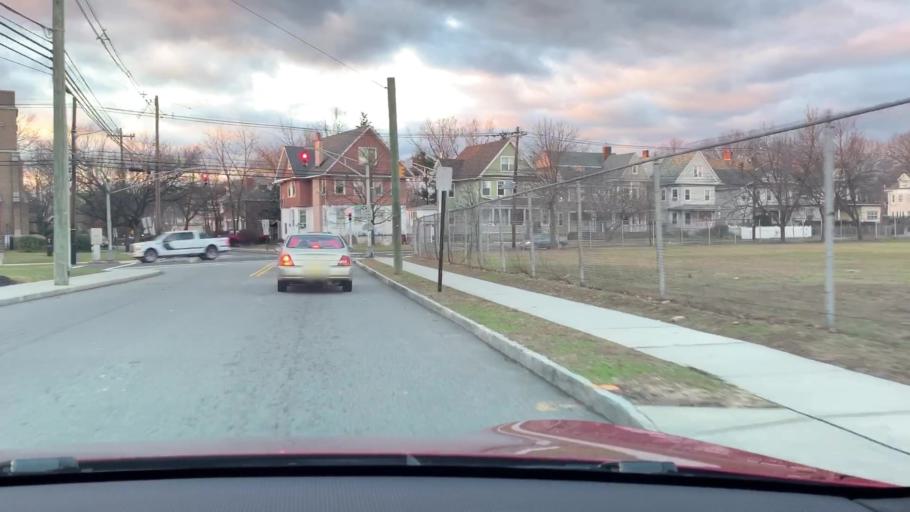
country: US
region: New Jersey
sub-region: Bergen County
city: Englewood
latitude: 40.8996
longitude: -73.9764
